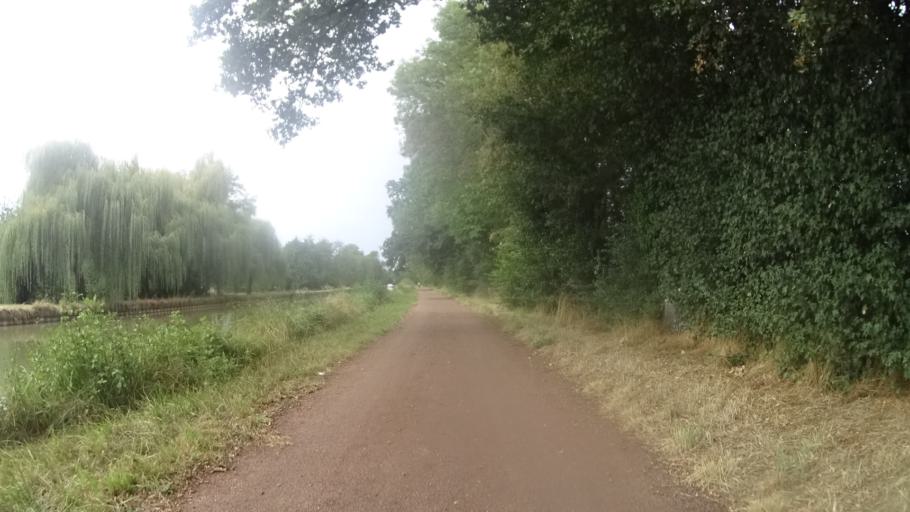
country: FR
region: Bourgogne
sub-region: Departement de la Nievre
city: Imphy
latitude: 46.9209
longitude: 3.2397
